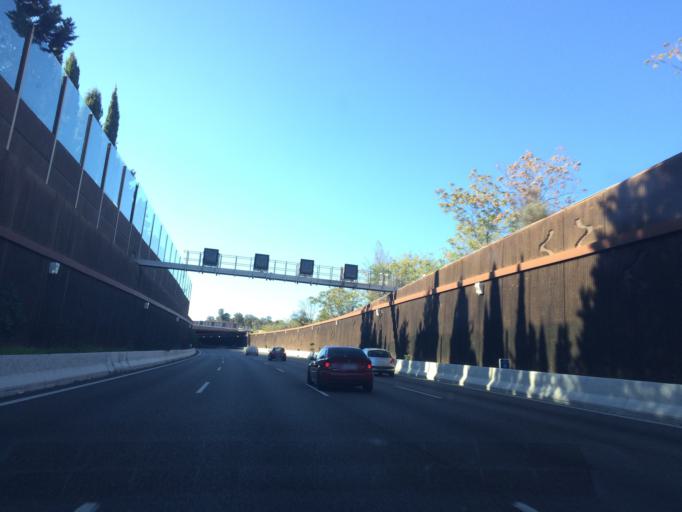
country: ES
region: Madrid
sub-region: Provincia de Madrid
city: El Pardo
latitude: 40.4737
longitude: -3.7669
